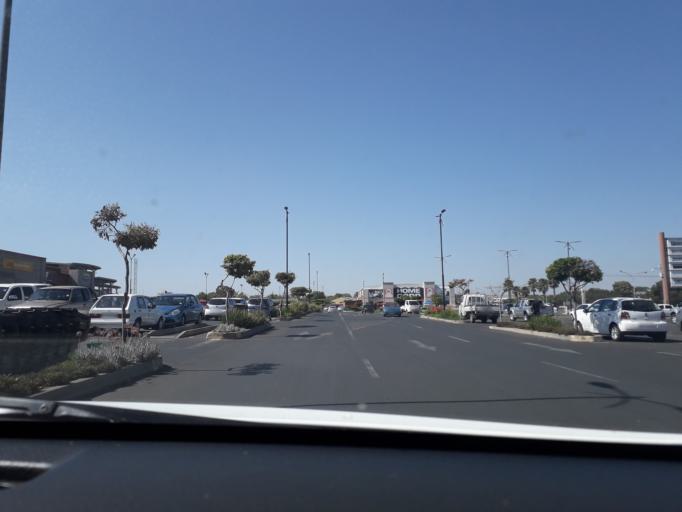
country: ZA
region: Gauteng
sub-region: City of Johannesburg Metropolitan Municipality
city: Modderfontein
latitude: -26.1057
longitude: 28.2225
